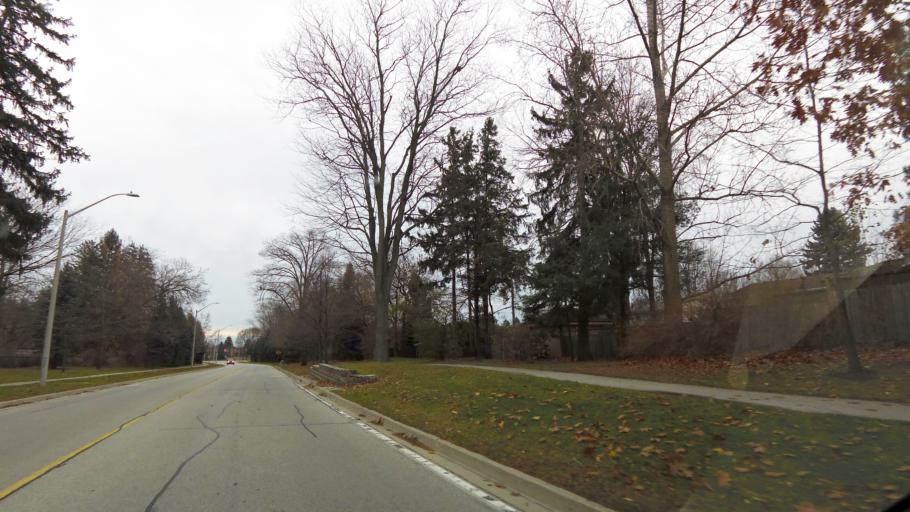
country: CA
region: Ontario
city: Oakville
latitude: 43.4778
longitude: -79.6381
